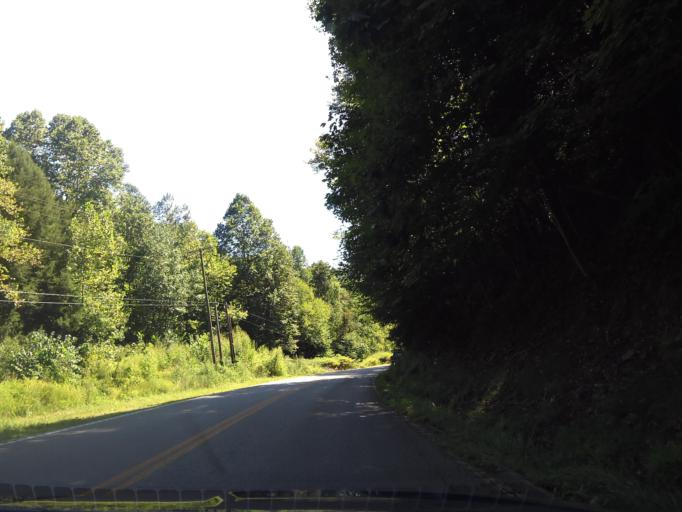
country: US
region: Kentucky
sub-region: Leslie County
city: Hyden
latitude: 37.1545
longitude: -83.5034
